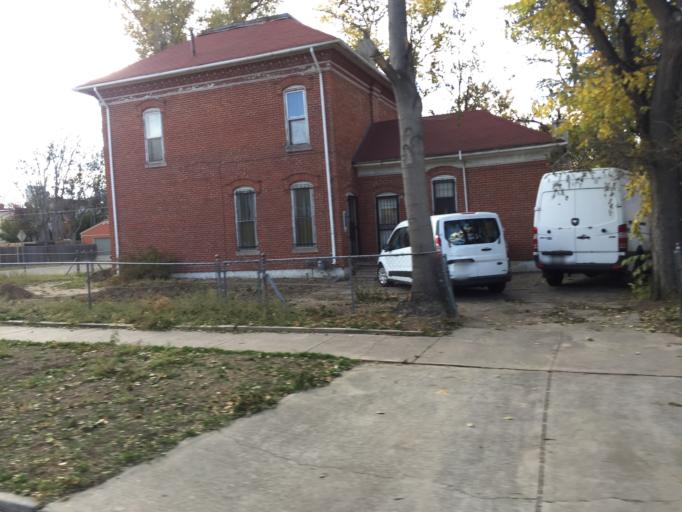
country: US
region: Colorado
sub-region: Denver County
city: Denver
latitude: 39.7586
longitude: -104.9684
